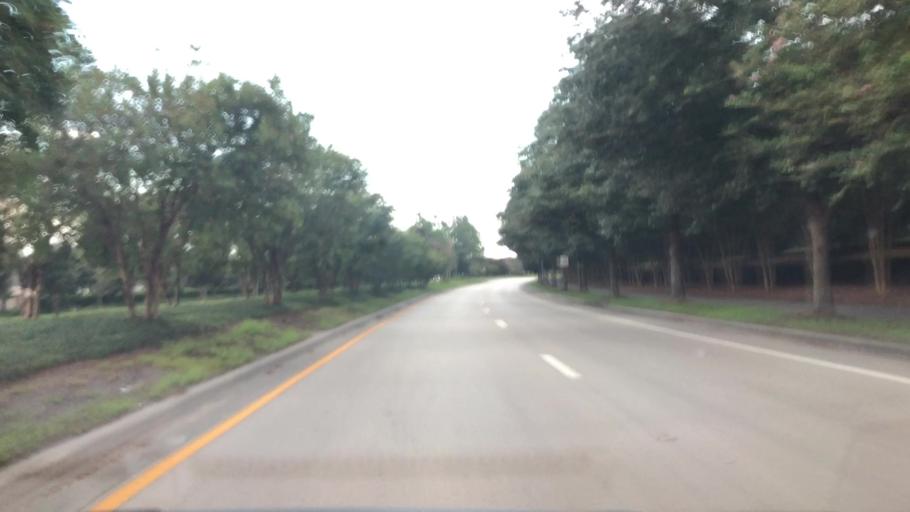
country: US
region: Florida
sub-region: Saint Johns County
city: Palm Valley
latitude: 30.0989
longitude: -81.4521
